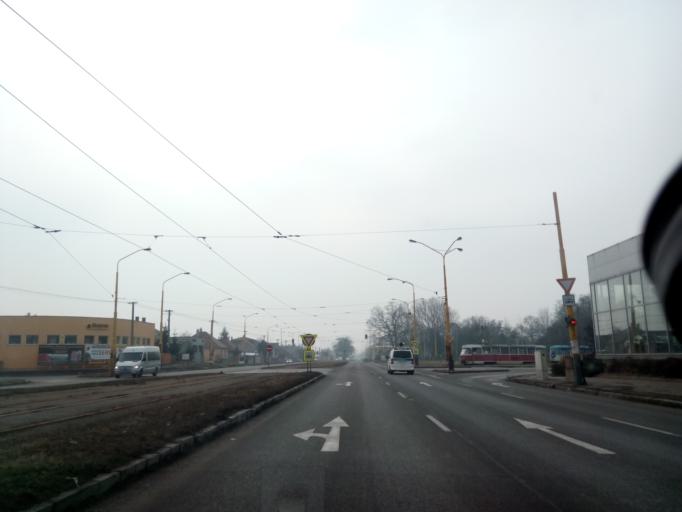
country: SK
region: Kosicky
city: Kosice
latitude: 48.6804
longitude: 21.2683
